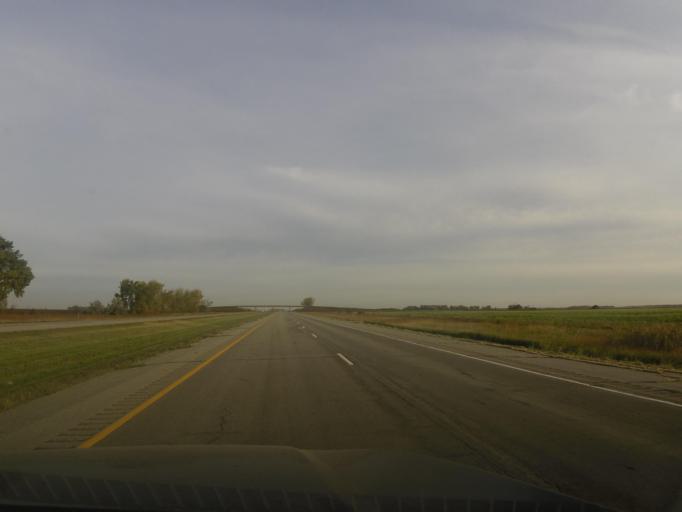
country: US
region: Minnesota
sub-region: Kittson County
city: Hallock
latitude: 48.7268
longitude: -97.1955
